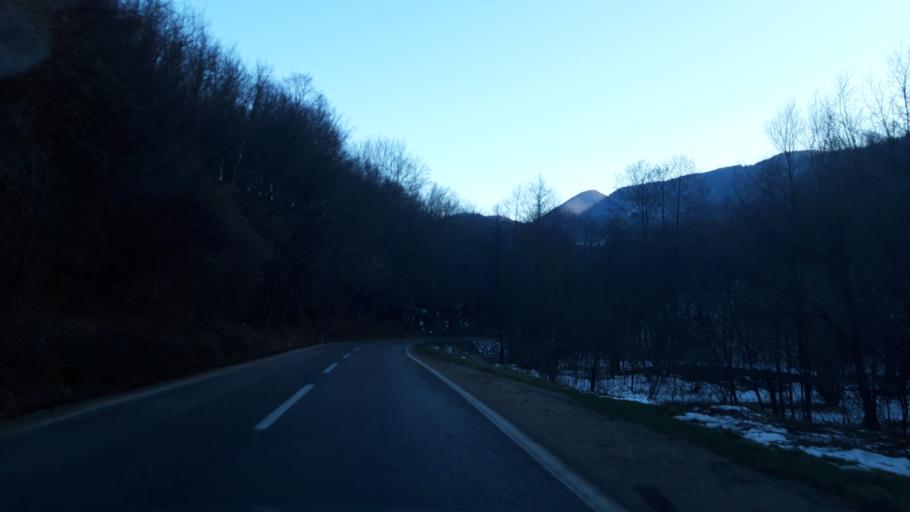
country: BA
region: Republika Srpska
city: Vlasenica
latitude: 44.1754
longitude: 19.0122
